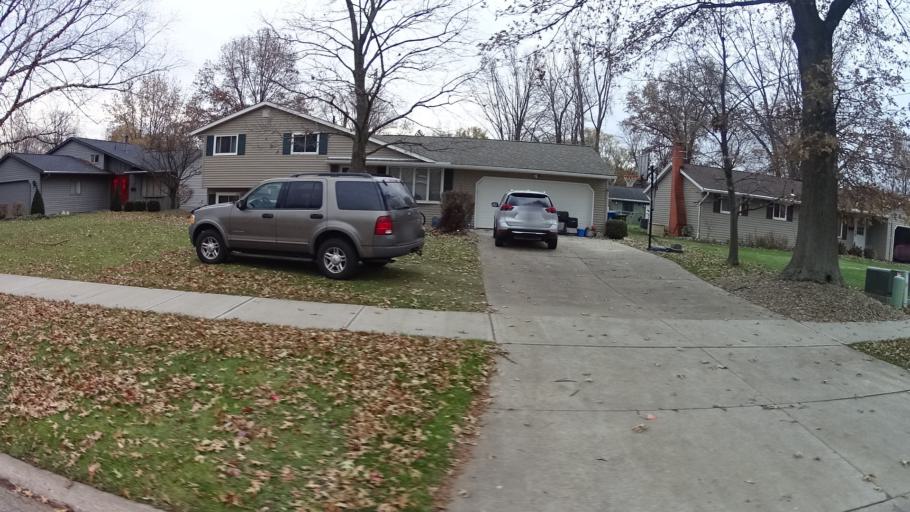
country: US
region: Ohio
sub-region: Lorain County
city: North Ridgeville
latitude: 41.4031
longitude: -82.0016
